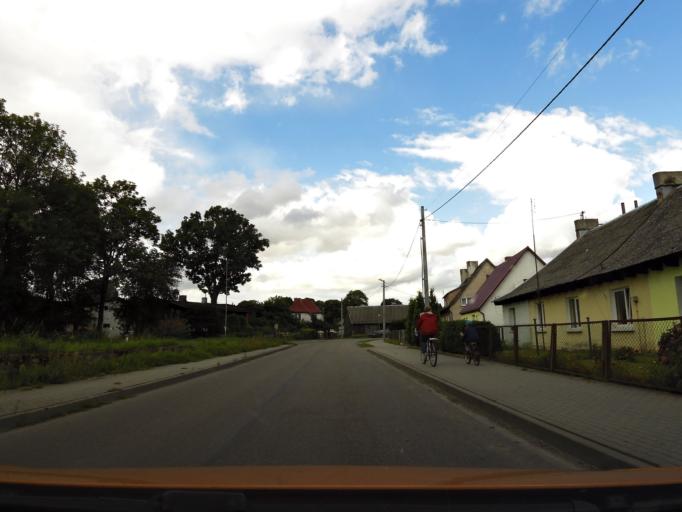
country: PL
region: West Pomeranian Voivodeship
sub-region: Powiat kolobrzeski
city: Ryman
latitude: 53.9981
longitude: 15.4931
